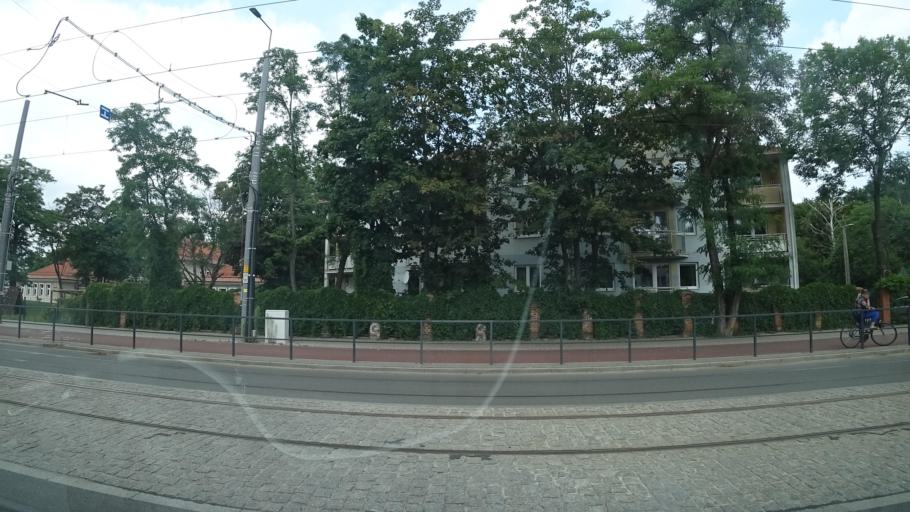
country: PL
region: Pomeranian Voivodeship
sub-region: Gdansk
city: Gdansk
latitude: 54.3637
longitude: 18.7164
